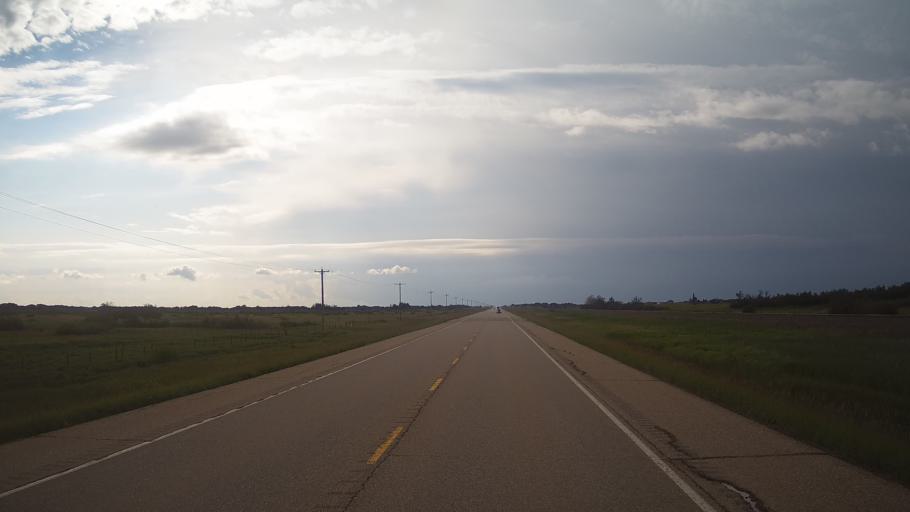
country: CA
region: Alberta
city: Viking
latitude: 53.1411
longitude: -111.9395
